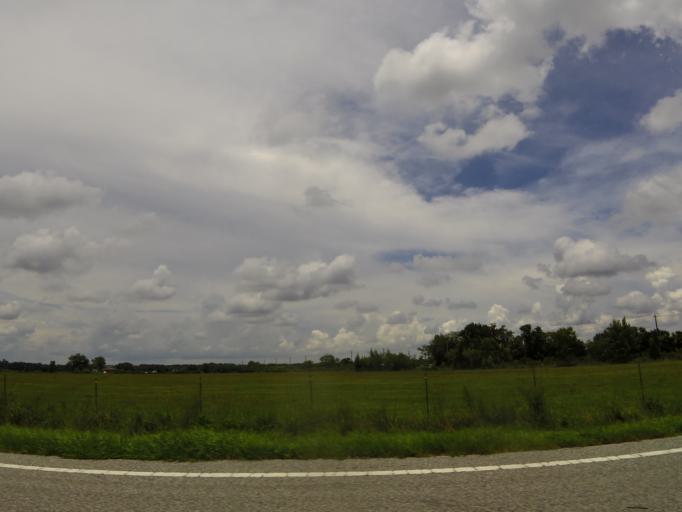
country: US
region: Florida
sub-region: Putnam County
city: East Palatka
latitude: 29.6930
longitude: -81.4851
